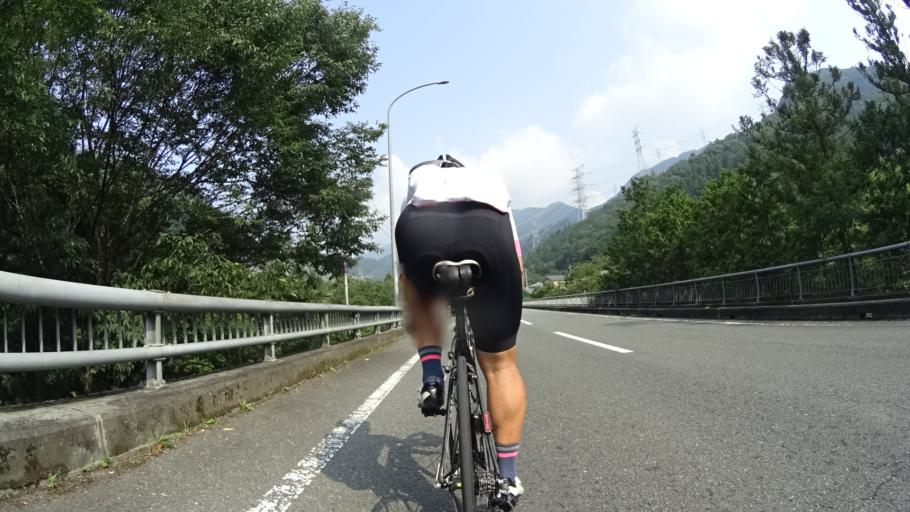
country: JP
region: Saitama
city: Chichibu
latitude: 36.0284
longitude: 138.9412
